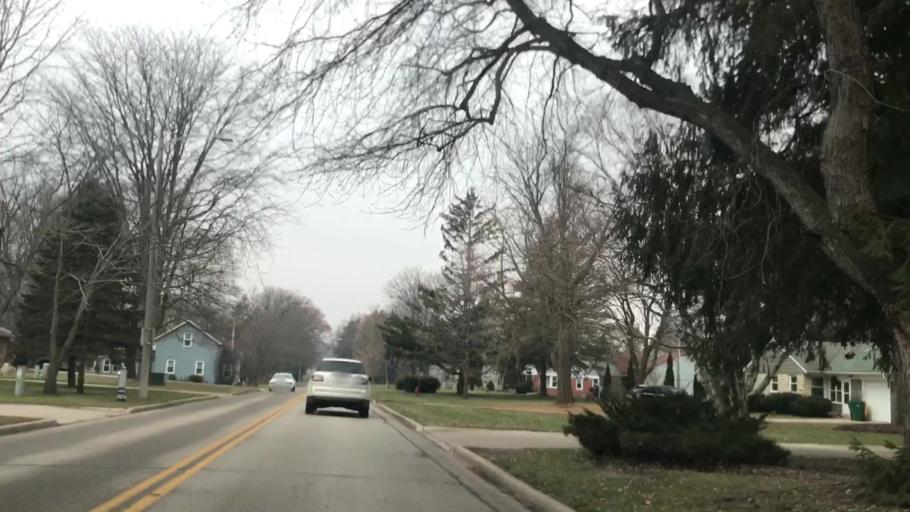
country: US
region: Wisconsin
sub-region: Ozaukee County
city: Thiensville
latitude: 43.2362
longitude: -87.9762
